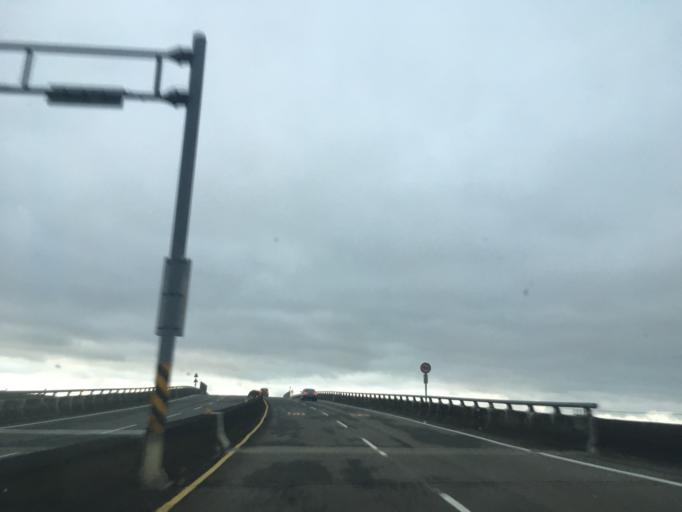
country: TW
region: Taiwan
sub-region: Miaoli
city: Miaoli
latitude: 24.4585
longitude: 120.7813
